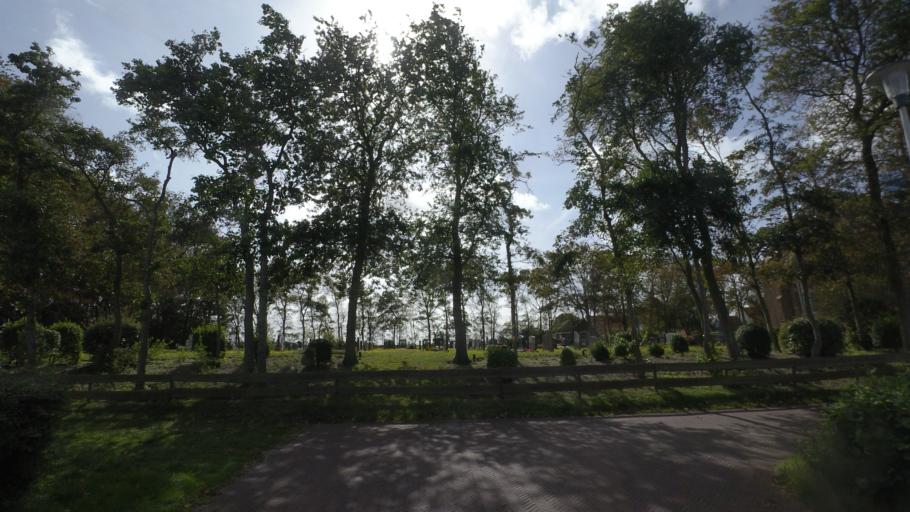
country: NL
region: Friesland
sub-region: Gemeente Ameland
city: Hollum
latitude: 53.4359
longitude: 5.6421
